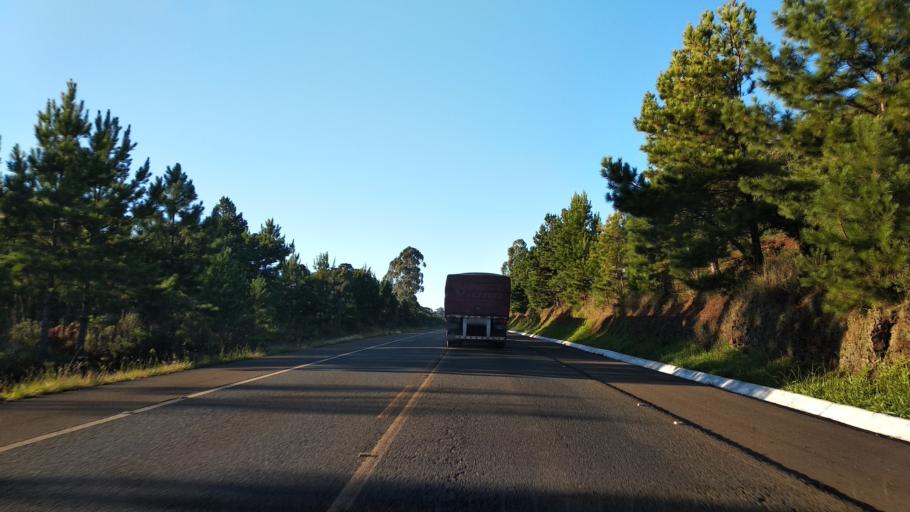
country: BR
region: Santa Catarina
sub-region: Correia Pinto
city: Correia Pinto
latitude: -27.6397
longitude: -50.5973
